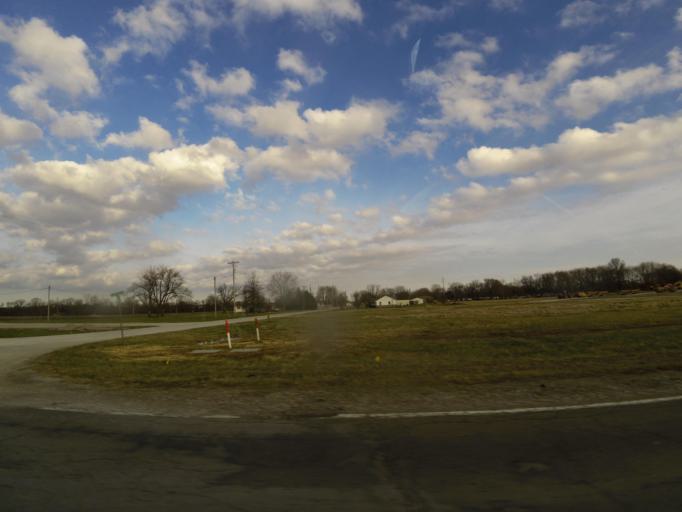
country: US
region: Illinois
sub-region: Bond County
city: Greenville
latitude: 38.9185
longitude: -89.2752
